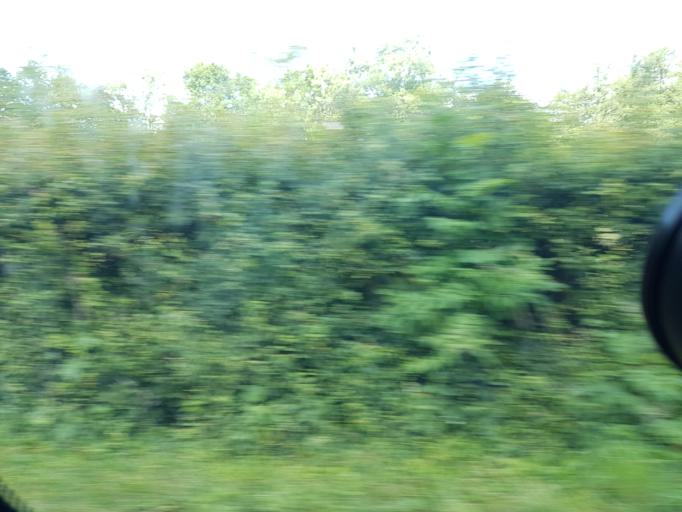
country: FR
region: Bourgogne
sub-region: Departement de Saone-et-Loire
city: Epinac
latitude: 46.9746
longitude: 4.5004
